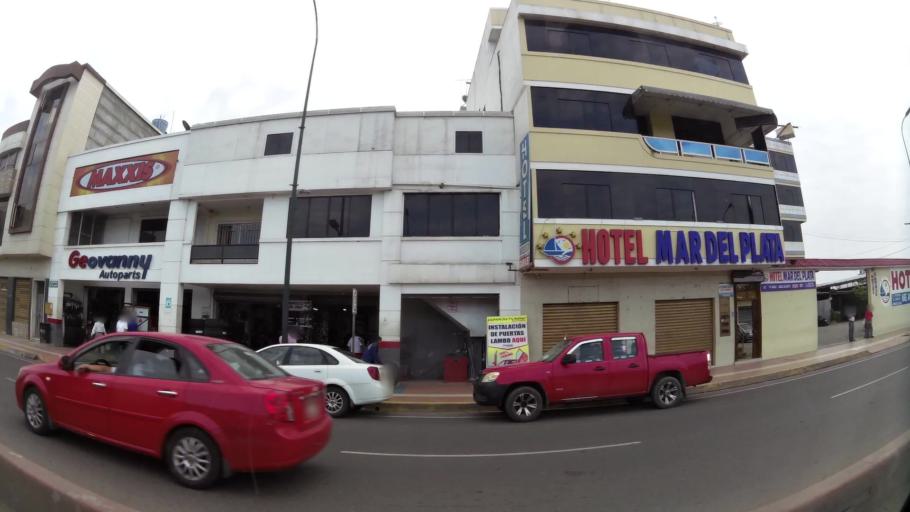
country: EC
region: El Oro
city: Machala
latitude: -3.2670
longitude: -79.9502
